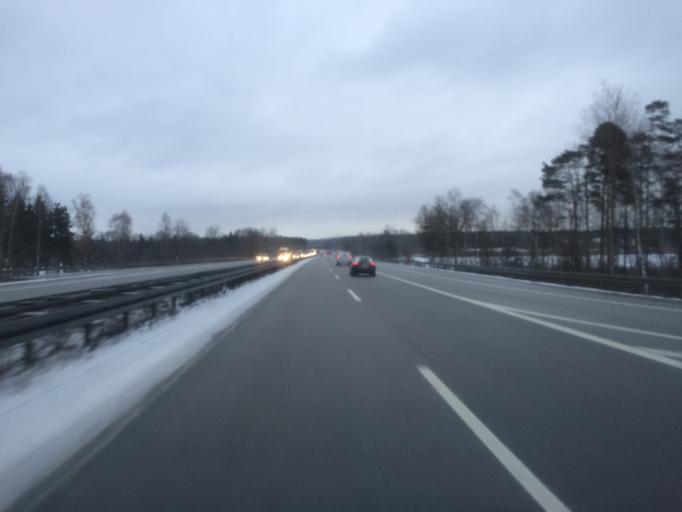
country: DE
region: Bavaria
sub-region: Upper Palatinate
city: Schwandorf in Bayern
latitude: 49.2745
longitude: 12.1292
